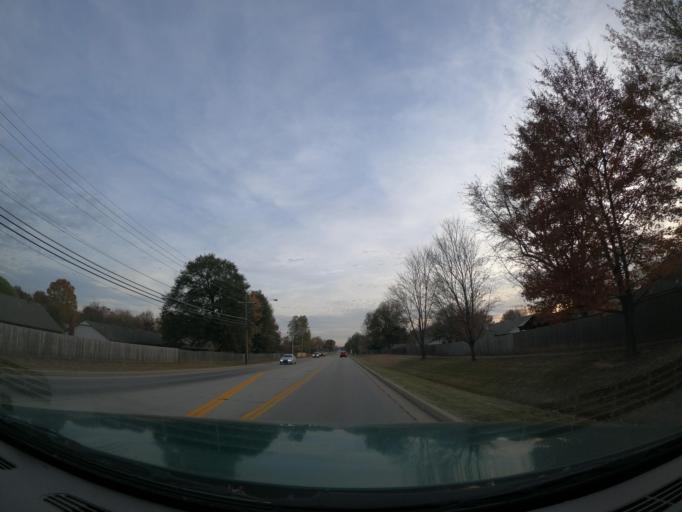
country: US
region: Oklahoma
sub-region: Tulsa County
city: Broken Arrow
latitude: 35.9837
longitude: -95.7974
